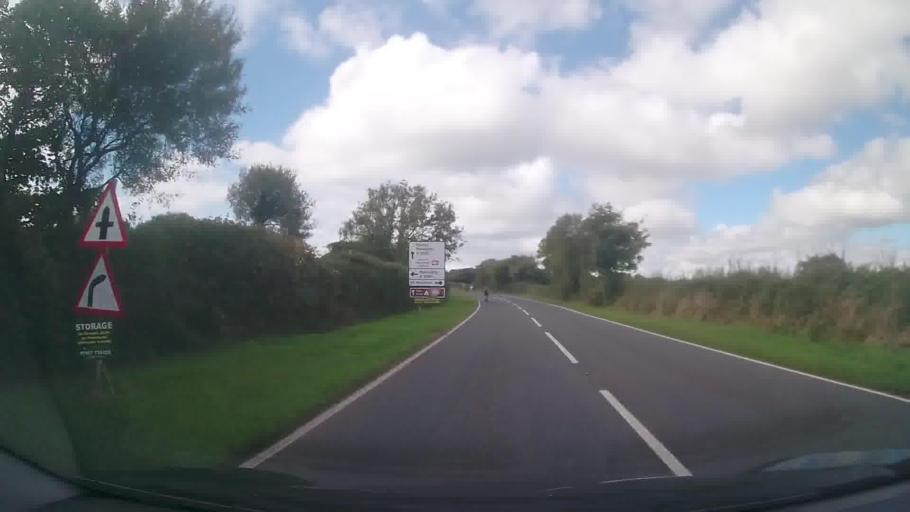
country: GB
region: Wales
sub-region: Pembrokeshire
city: Manorbier
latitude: 51.6516
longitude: -4.7775
